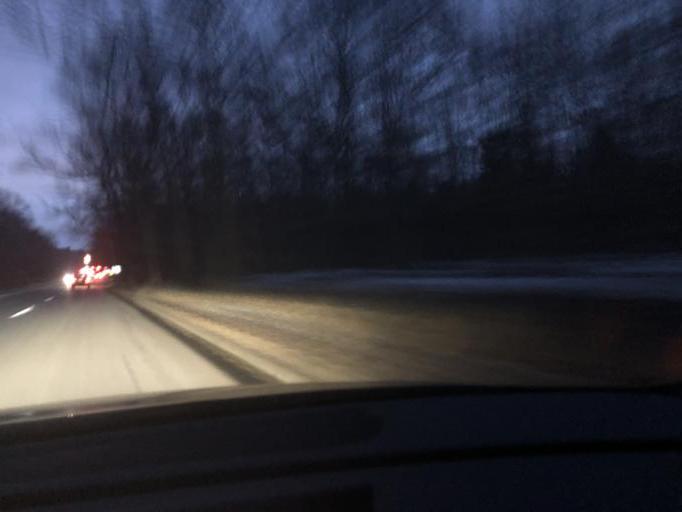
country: US
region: New Jersey
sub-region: Essex County
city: Northfield
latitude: 40.7646
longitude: -74.3352
